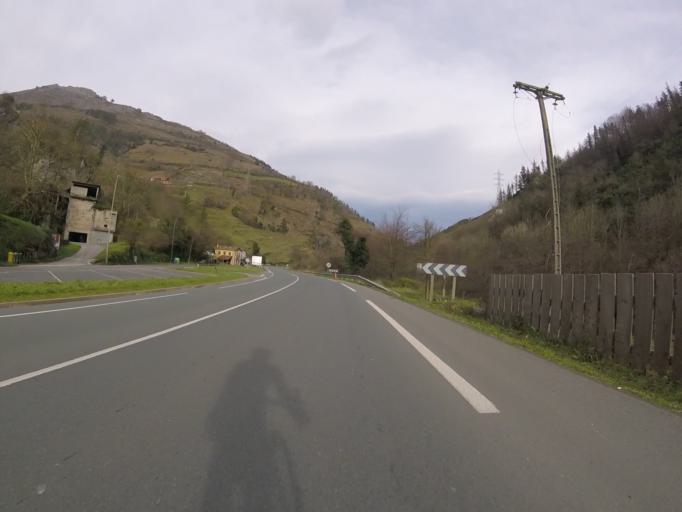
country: ES
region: Basque Country
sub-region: Provincia de Guipuzcoa
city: Azpeitia
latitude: 43.1910
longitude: -2.2587
